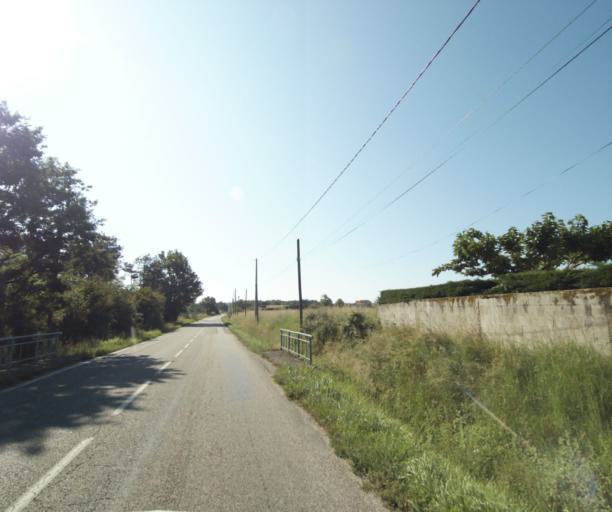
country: FR
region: Midi-Pyrenees
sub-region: Departement du Tarn-et-Garonne
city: Saint-Nauphary
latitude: 44.0035
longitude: 1.3987
